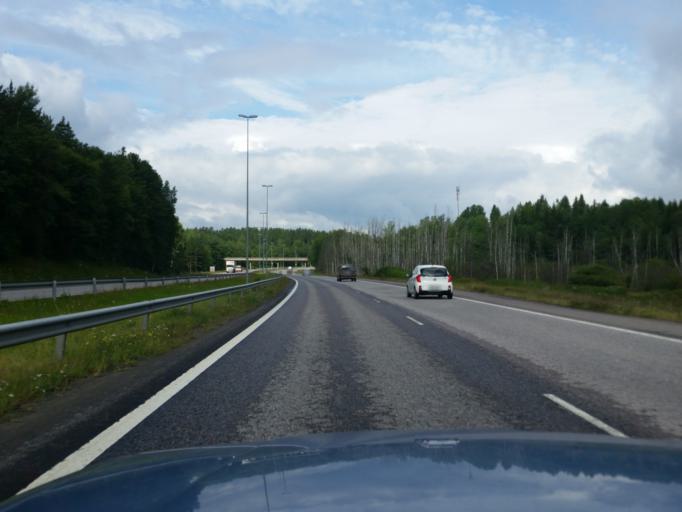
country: FI
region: Uusimaa
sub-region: Helsinki
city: Kirkkonummi
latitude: 60.2840
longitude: 24.4299
